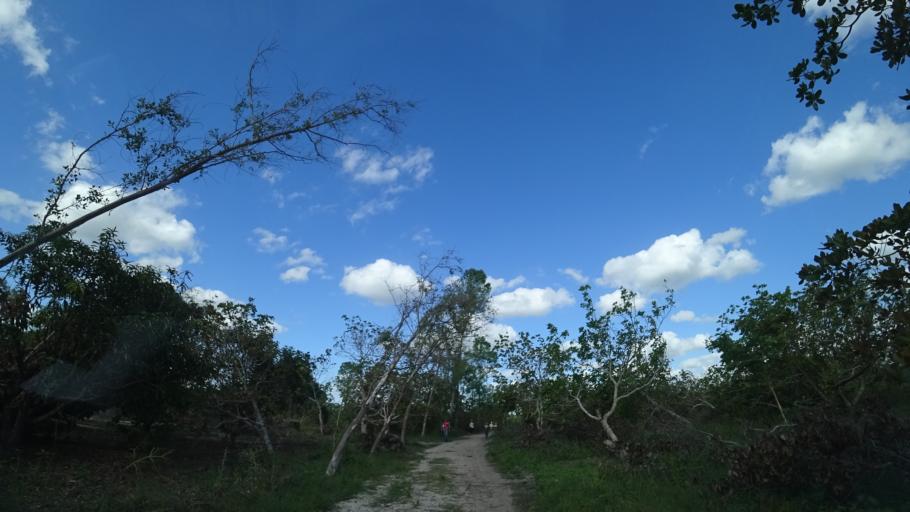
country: MZ
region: Sofala
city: Dondo
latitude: -19.4256
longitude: 34.7065
